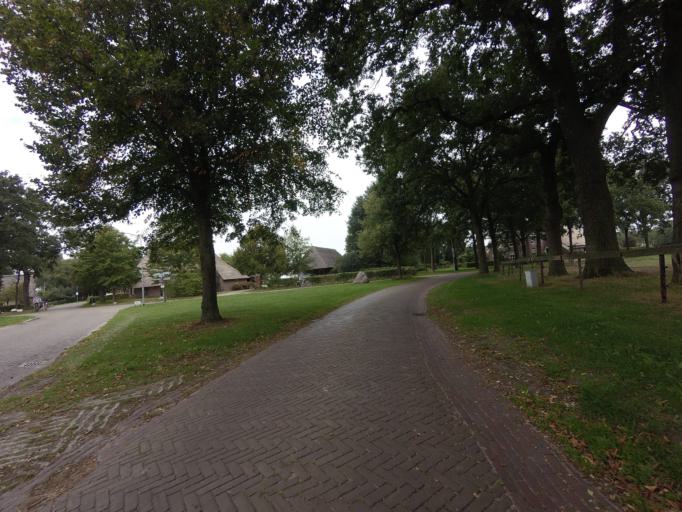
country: NL
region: Drenthe
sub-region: Gemeente Assen
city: Assen
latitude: 52.9958
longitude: 6.6319
